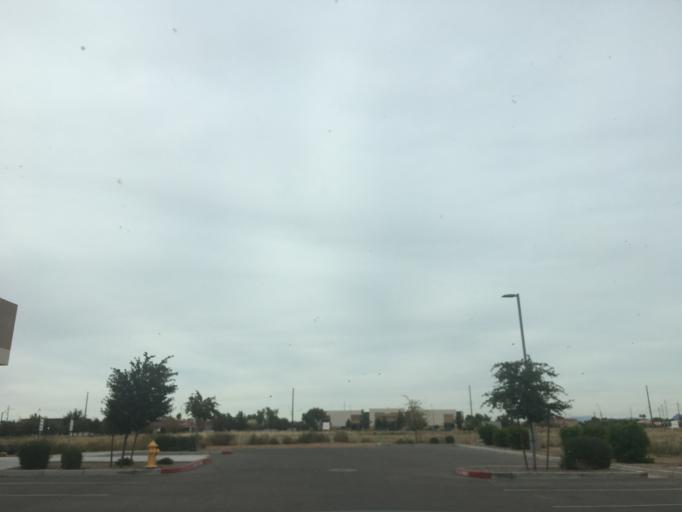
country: US
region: Arizona
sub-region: Maricopa County
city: San Carlos
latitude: 33.3476
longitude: -111.8274
